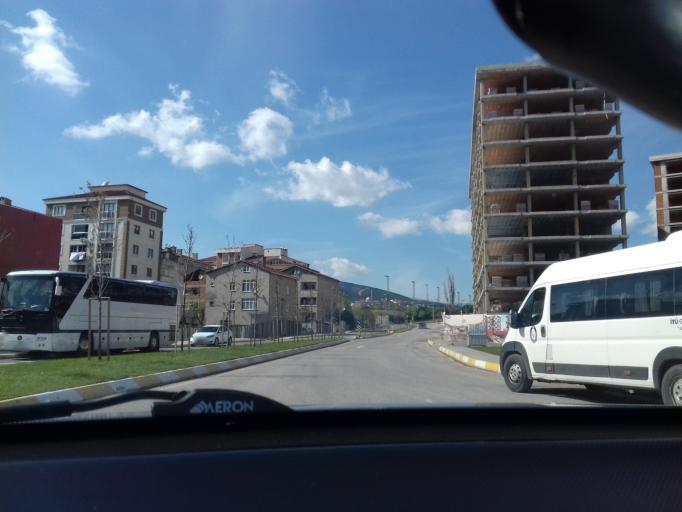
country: TR
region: Istanbul
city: Pendik
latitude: 40.8969
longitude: 29.2779
